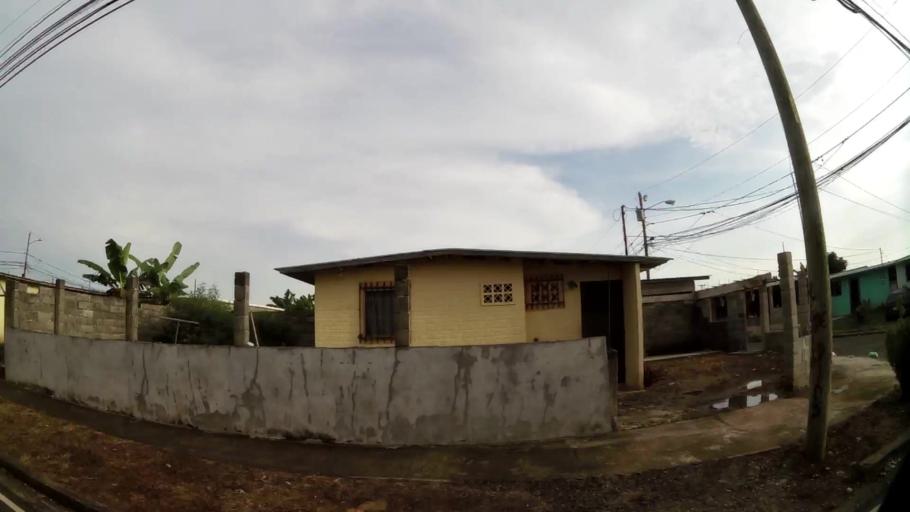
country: PA
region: Panama
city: Tocumen
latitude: 9.0803
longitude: -79.3604
